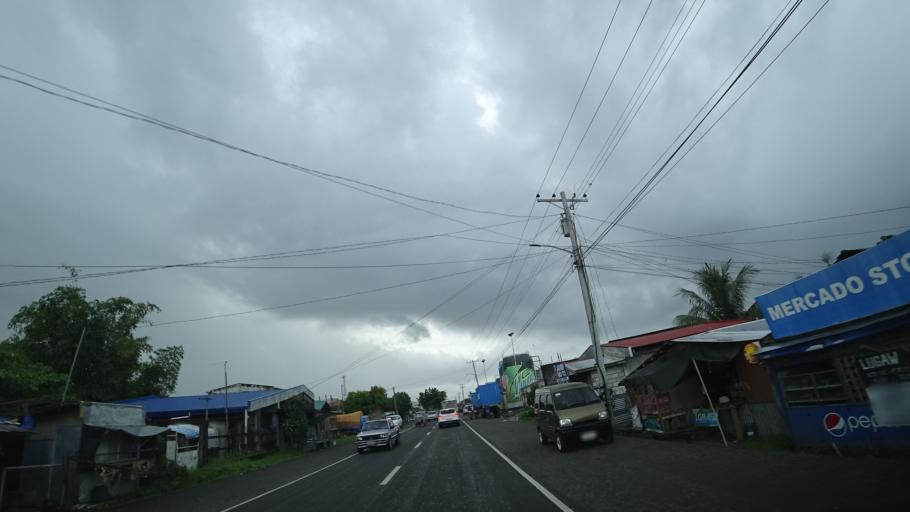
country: PH
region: Eastern Visayas
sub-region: Province of Leyte
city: Tolosa
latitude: 11.1014
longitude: 125.0194
